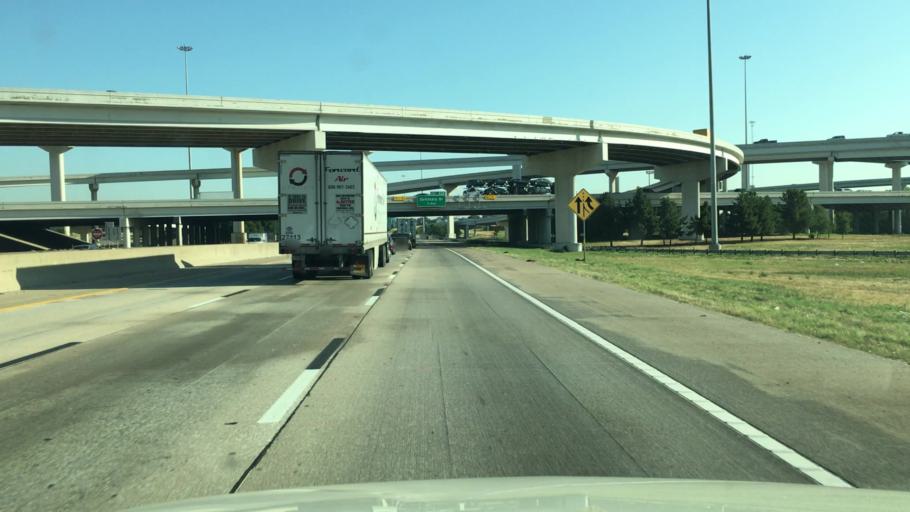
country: US
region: Texas
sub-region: Tarrant County
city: Edgecliff Village
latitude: 32.6655
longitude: -97.3207
